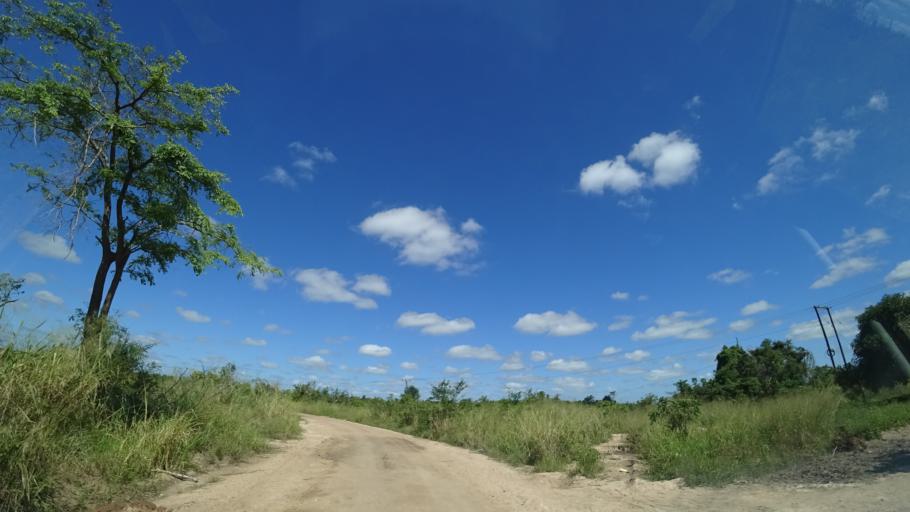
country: MZ
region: Sofala
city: Dondo
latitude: -19.3154
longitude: 34.6905
